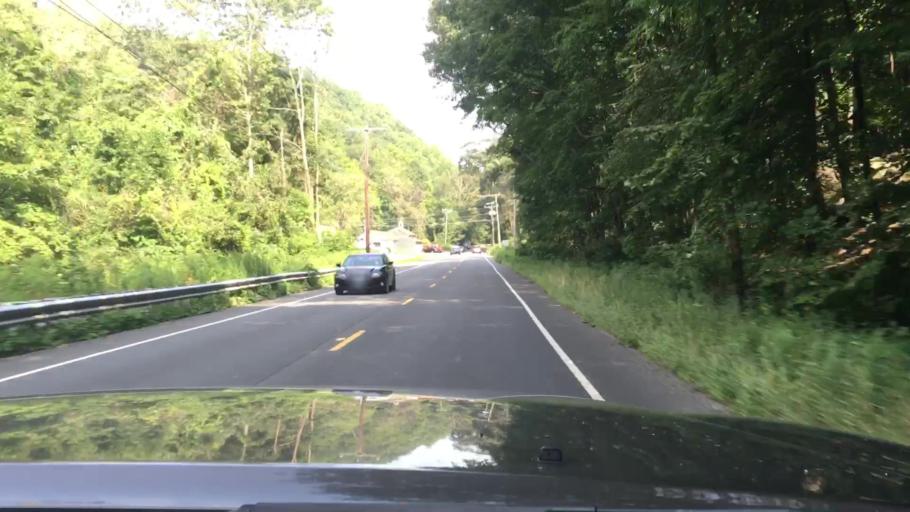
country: US
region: Connecticut
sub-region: Fairfield County
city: Georgetown
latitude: 41.2721
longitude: -73.4432
